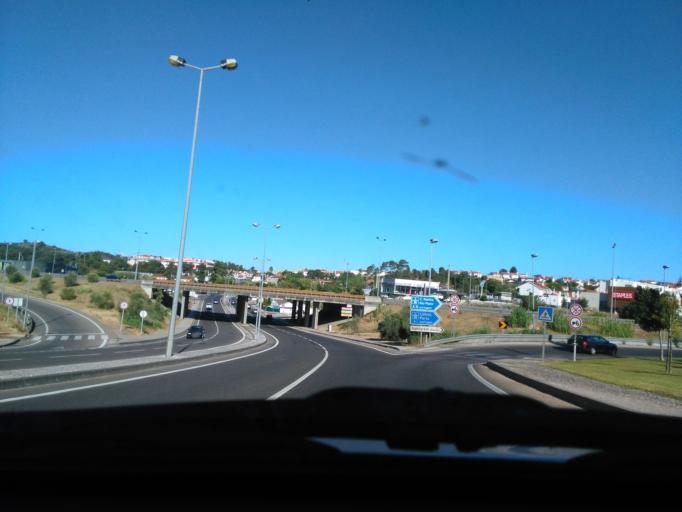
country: PT
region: Santarem
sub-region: Santarem
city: Santarem
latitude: 39.2394
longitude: -8.6995
